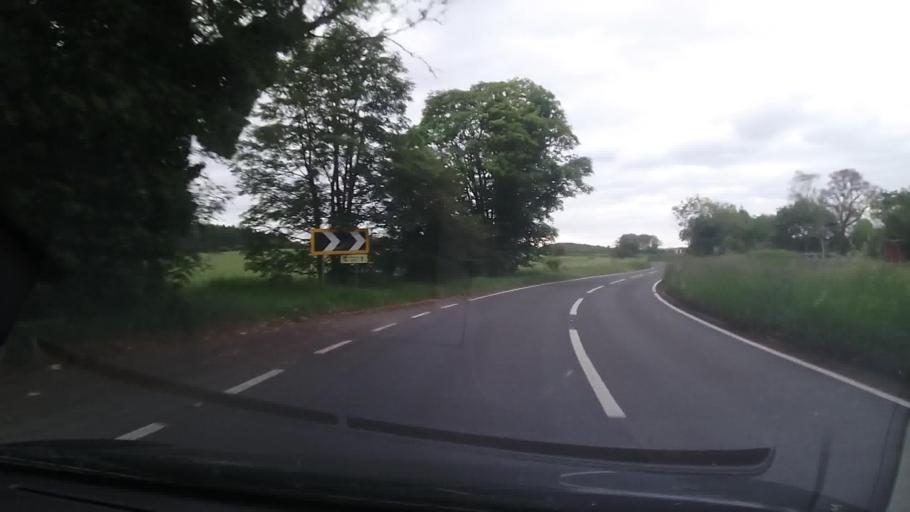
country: GB
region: England
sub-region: Shropshire
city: Clive
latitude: 52.7768
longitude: -2.7531
